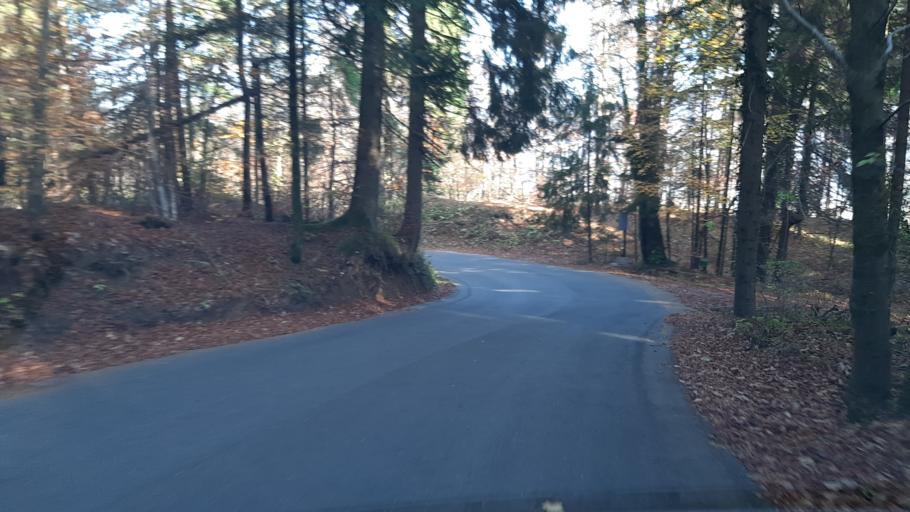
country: SI
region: Borovnica
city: Borovnica
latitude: 45.9006
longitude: 14.3633
